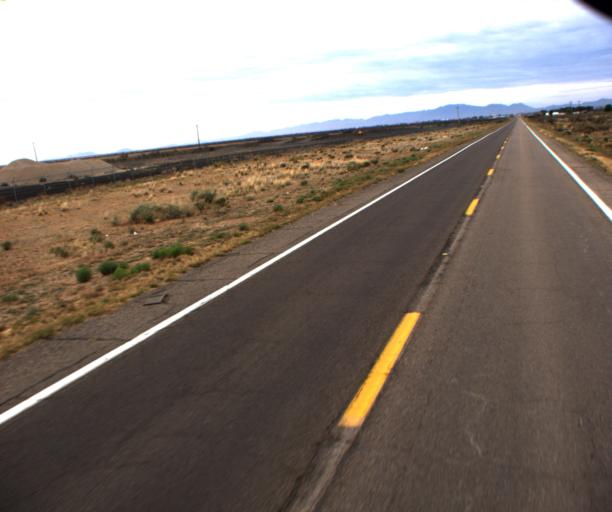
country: US
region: Arizona
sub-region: Cochise County
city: Willcox
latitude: 32.2964
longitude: -109.8021
